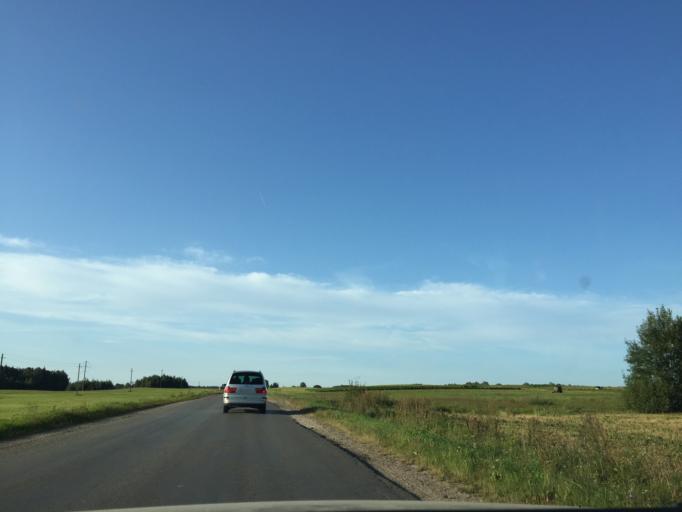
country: LT
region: Panevezys
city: Rokiskis
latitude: 55.9155
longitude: 25.6277
